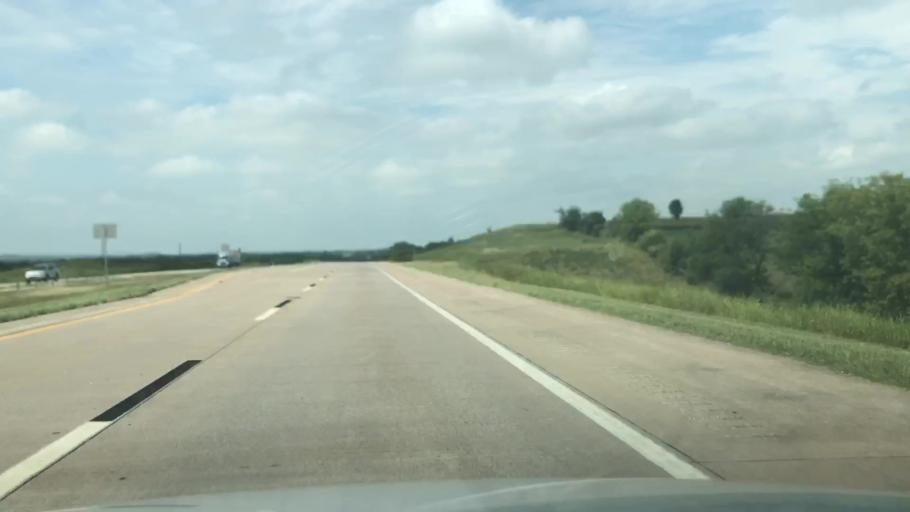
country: US
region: Oklahoma
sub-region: Osage County
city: Skiatook
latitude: 36.5186
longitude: -95.9231
